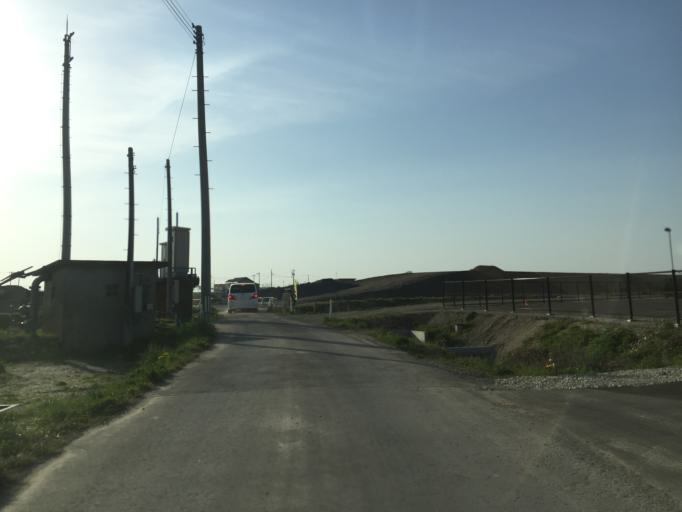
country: JP
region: Miyagi
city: Watari
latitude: 38.0240
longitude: 140.9027
